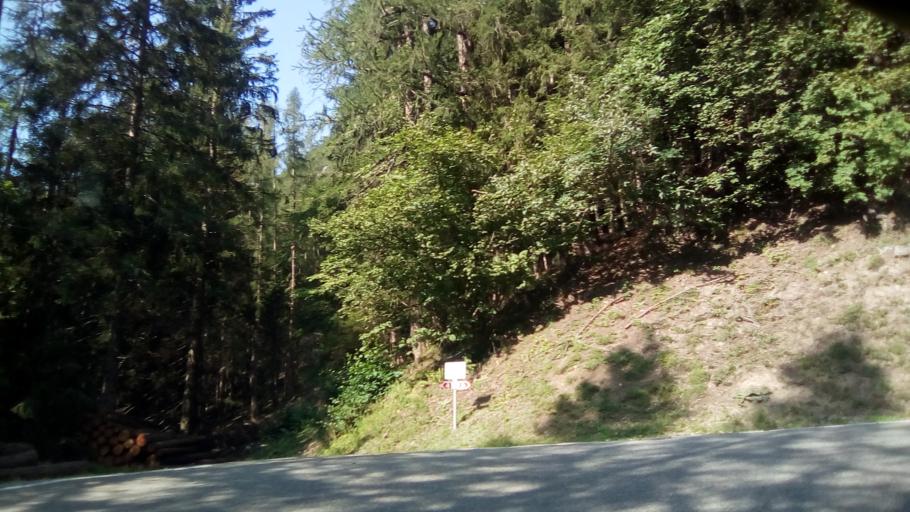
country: CH
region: Valais
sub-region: Martigny District
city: Martigny-Combe
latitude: 46.0543
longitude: 7.0836
